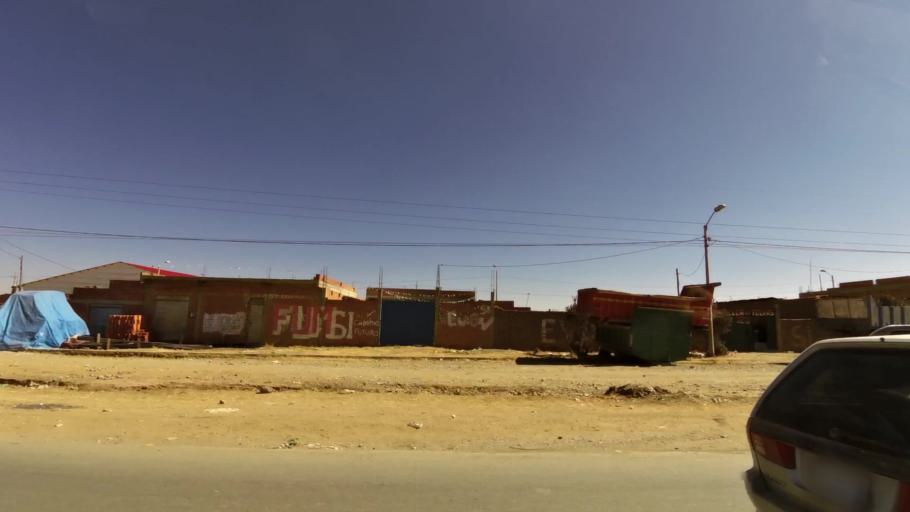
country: BO
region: La Paz
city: La Paz
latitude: -16.5730
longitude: -68.2262
